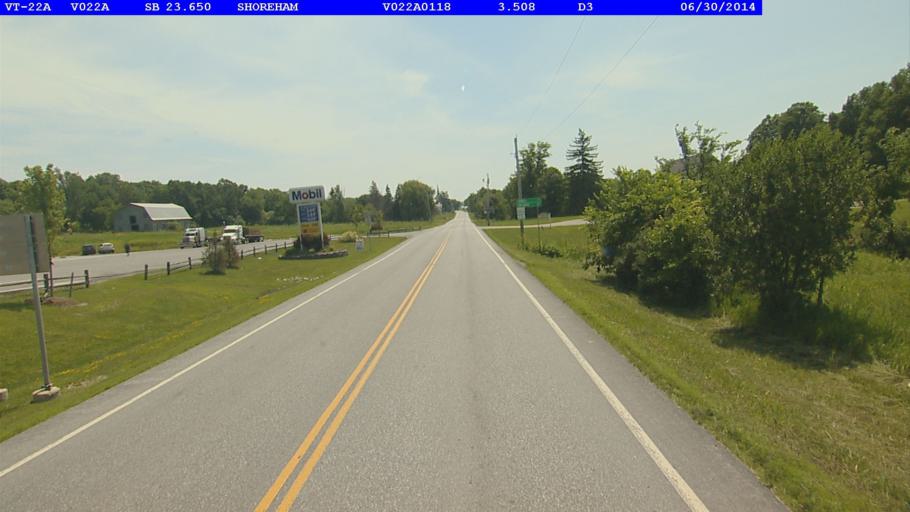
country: US
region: New York
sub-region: Essex County
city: Ticonderoga
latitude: 43.9000
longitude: -73.3083
